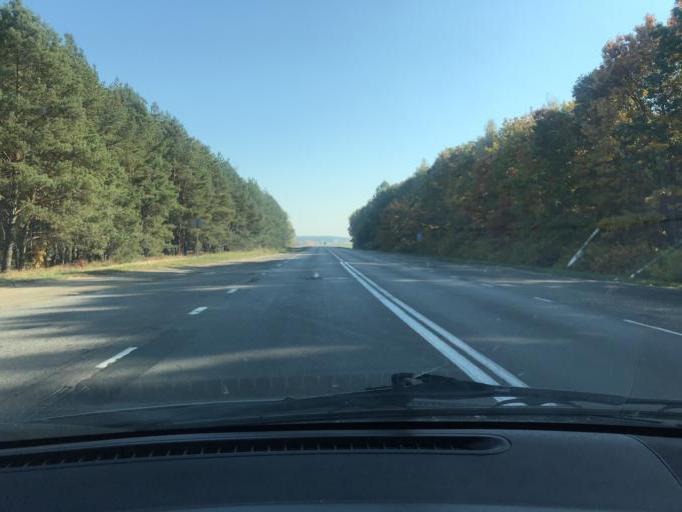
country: BY
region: Brest
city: Luninyets
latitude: 52.2770
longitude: 26.9587
